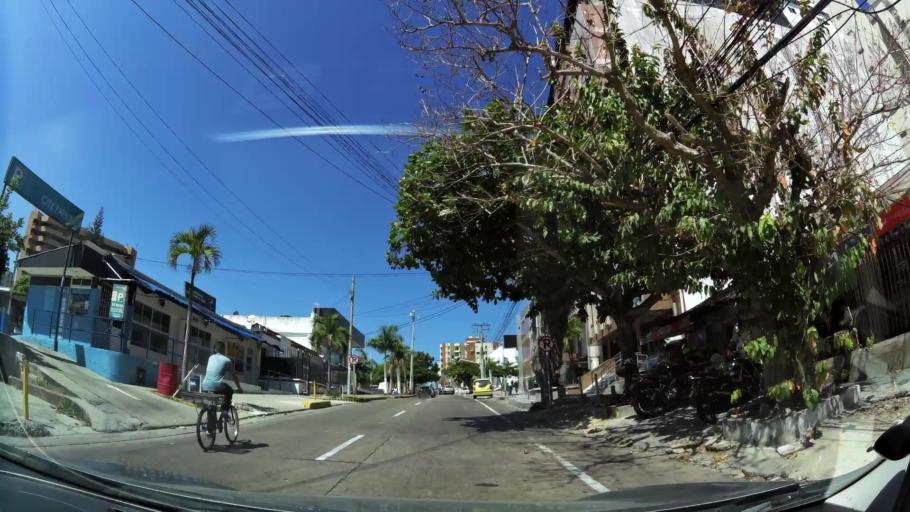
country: CO
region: Atlantico
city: Barranquilla
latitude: 11.0010
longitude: -74.8159
